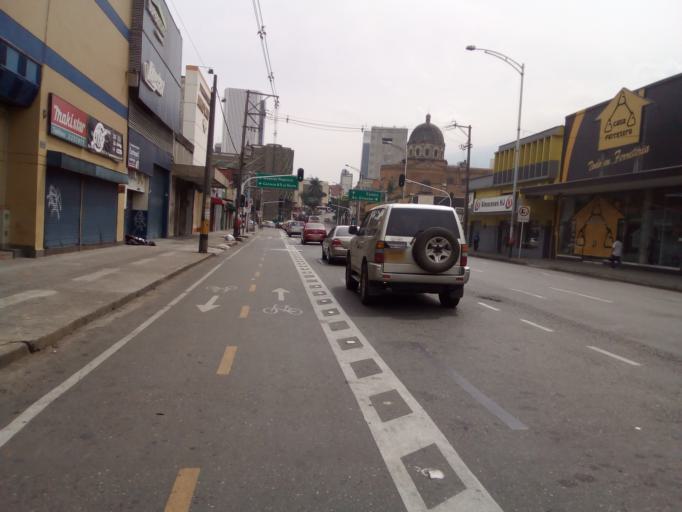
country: CO
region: Antioquia
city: Medellin
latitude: 6.2432
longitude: -75.5704
